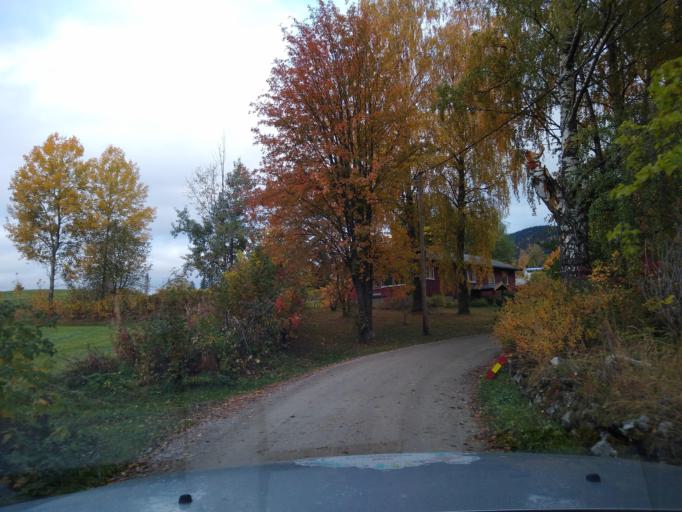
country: NO
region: Oppland
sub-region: Ringebu
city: Ringebu
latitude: 61.5415
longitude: 10.1288
